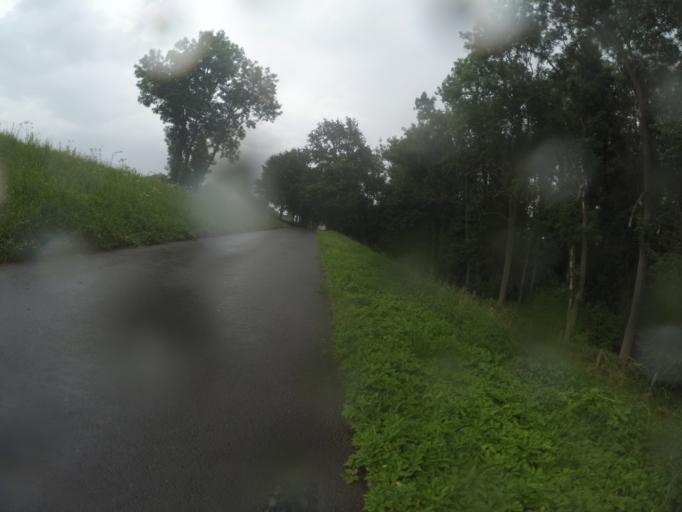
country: CZ
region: Central Bohemia
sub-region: Okres Melnik
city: Melnik
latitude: 50.3398
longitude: 14.4687
